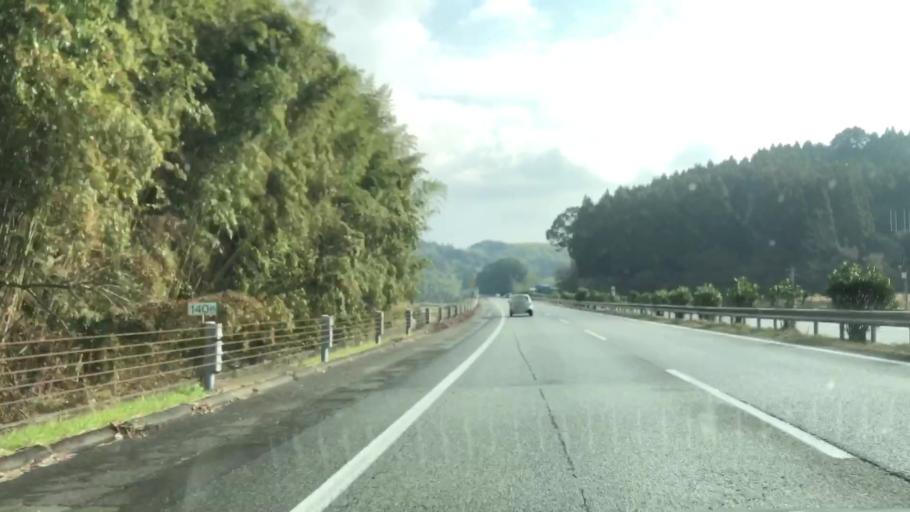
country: JP
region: Kumamoto
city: Yamaga
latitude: 33.0312
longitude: 130.5740
